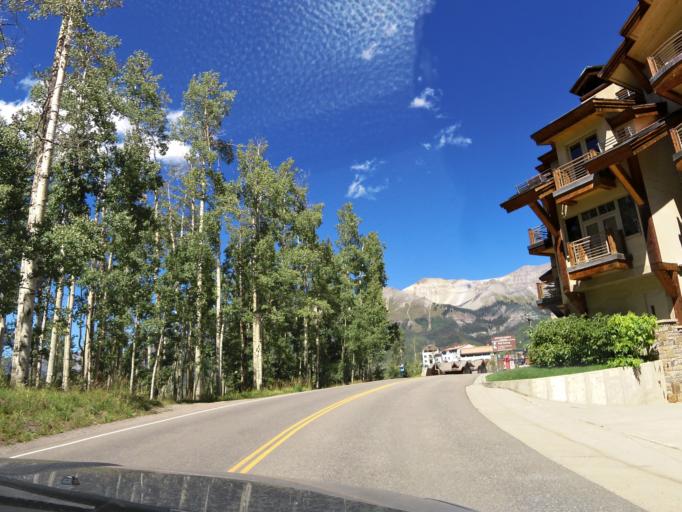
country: US
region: Colorado
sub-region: San Miguel County
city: Mountain Village
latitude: 37.9356
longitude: -107.8480
